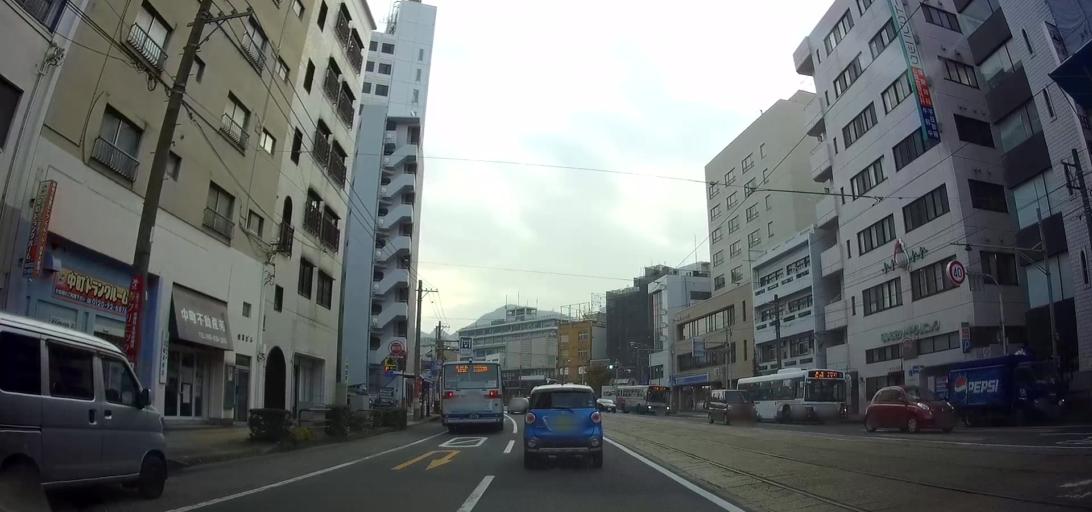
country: JP
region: Nagasaki
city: Nagasaki-shi
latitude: 32.7509
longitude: 129.8753
